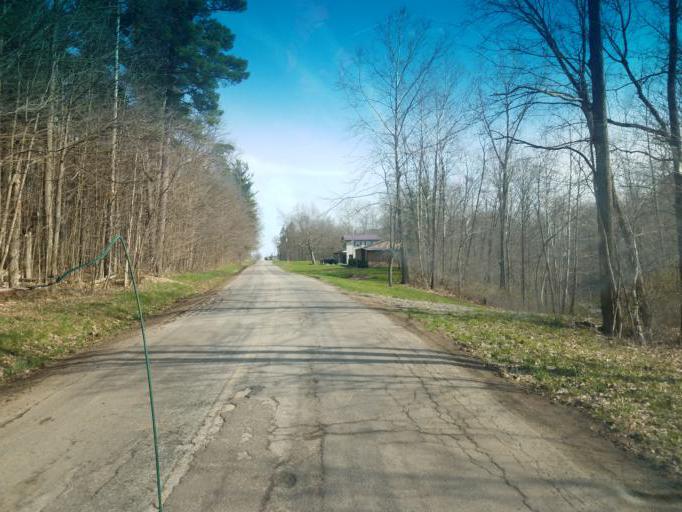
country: US
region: Ohio
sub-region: Richland County
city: Lincoln Heights
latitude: 40.8856
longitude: -82.4747
